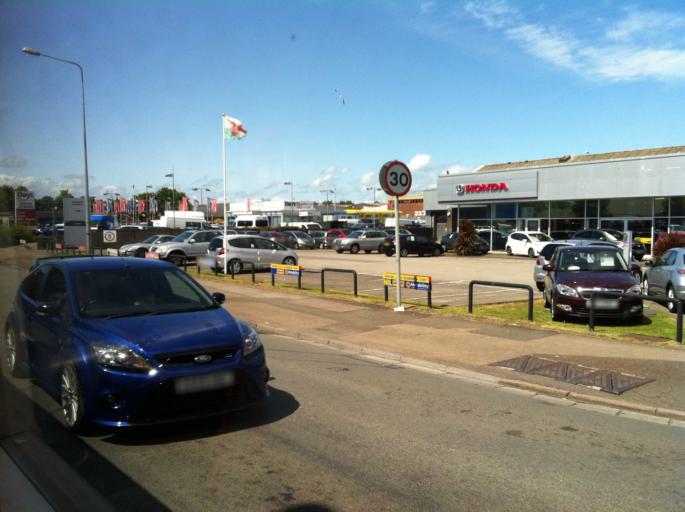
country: GB
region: Wales
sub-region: Cardiff
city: Cardiff
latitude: 51.4640
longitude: -3.1937
